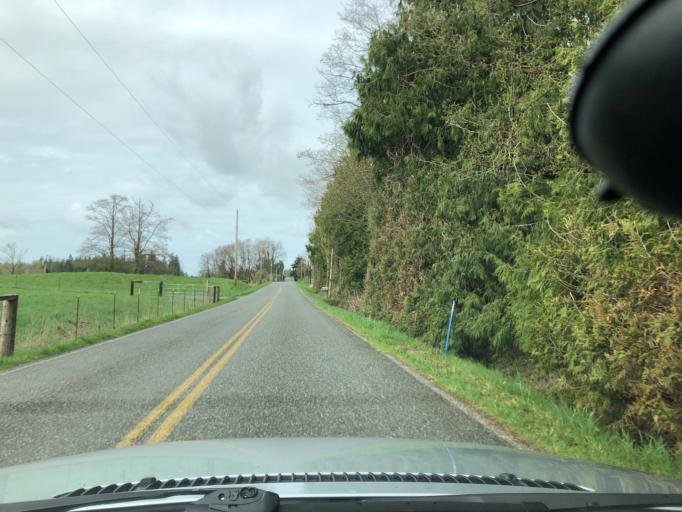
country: CA
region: British Columbia
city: Langley
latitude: 48.9795
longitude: -122.5614
